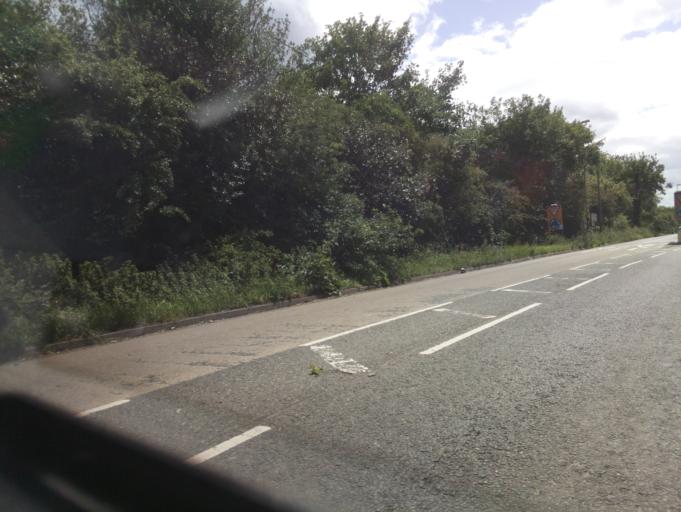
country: GB
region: England
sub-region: Nottinghamshire
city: Arnold
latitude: 53.0016
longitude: -1.1013
